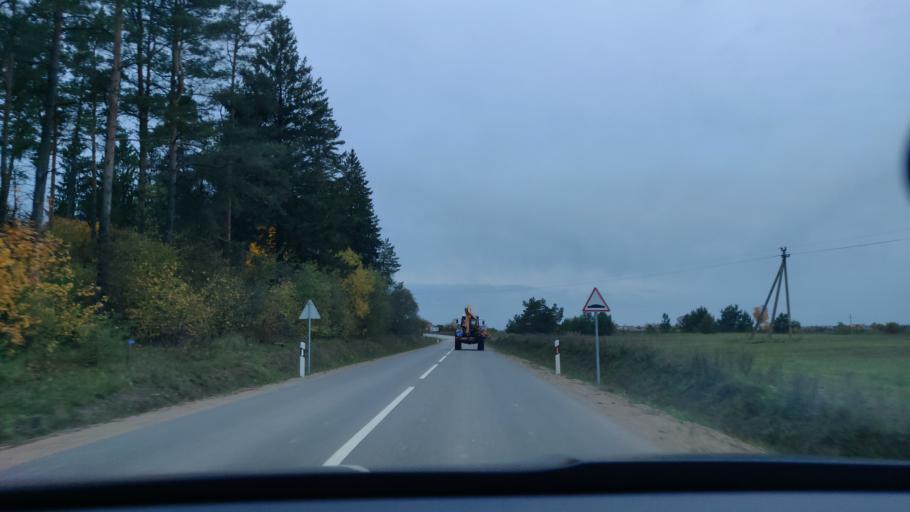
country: LT
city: Lentvaris
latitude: 54.5991
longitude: 25.0237
